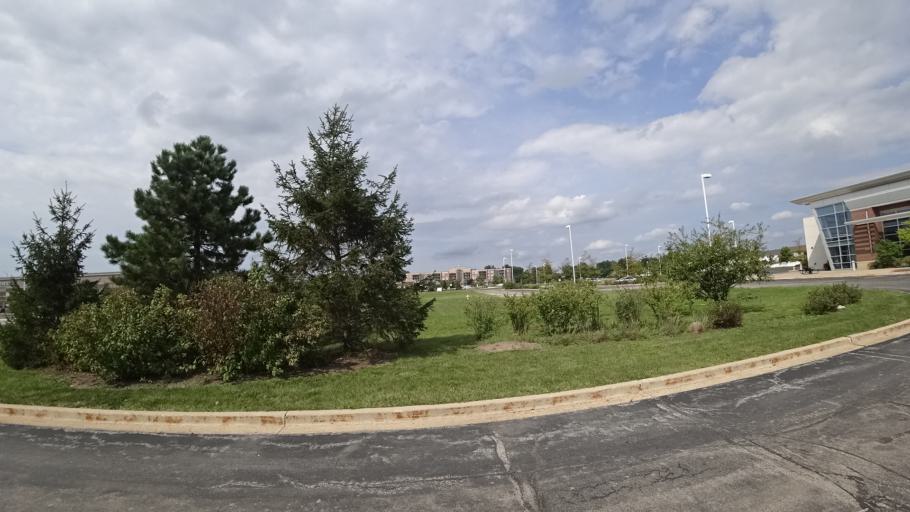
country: US
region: Illinois
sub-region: Cook County
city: Tinley Park
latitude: 41.5560
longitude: -87.7901
